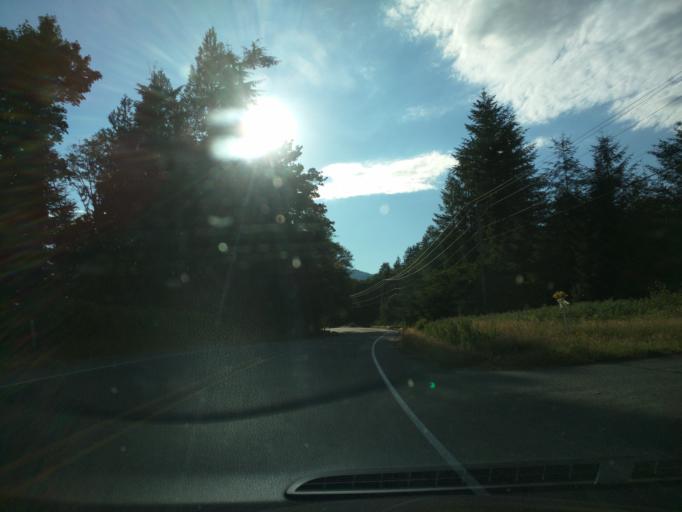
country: US
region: Washington
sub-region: Snohomish County
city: Arlington Heights
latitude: 48.2696
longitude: -121.9688
